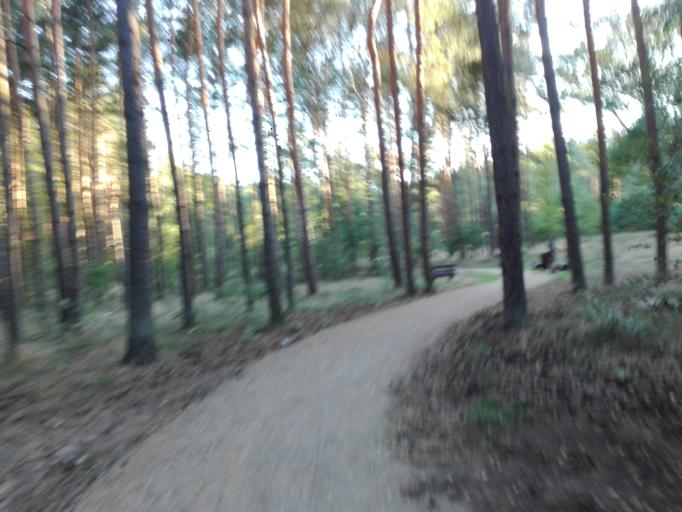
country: PL
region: West Pomeranian Voivodeship
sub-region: Powiat policki
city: Dobra
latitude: 53.4828
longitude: 14.3776
